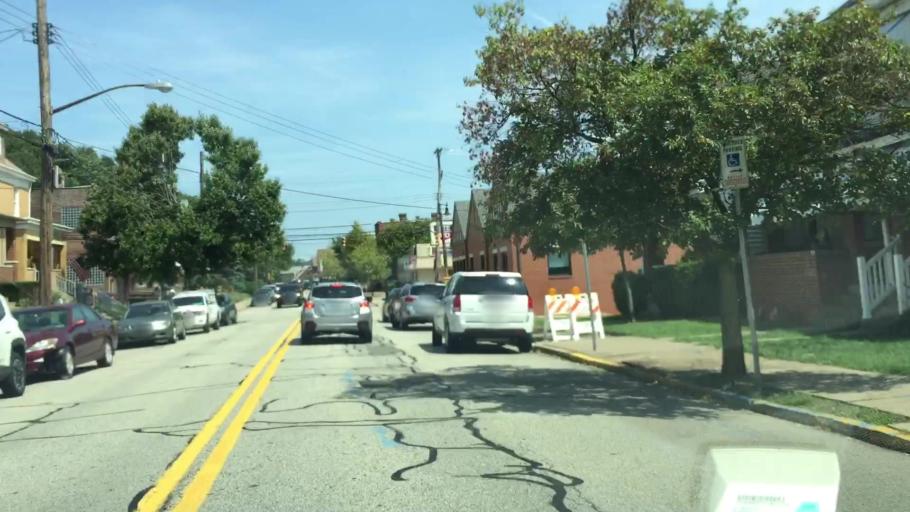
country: US
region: Pennsylvania
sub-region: Allegheny County
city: Sharpsburg
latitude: 40.4860
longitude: -79.9278
